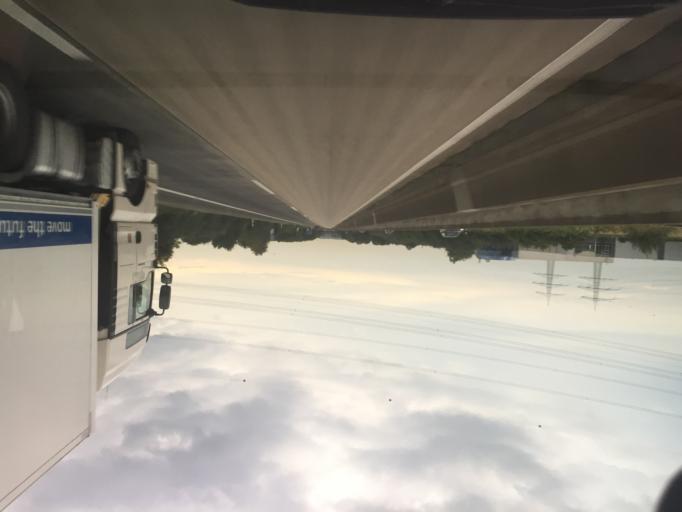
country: DE
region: North Rhine-Westphalia
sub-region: Regierungsbezirk Koln
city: Elsdorf
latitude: 50.9505
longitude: 6.5962
